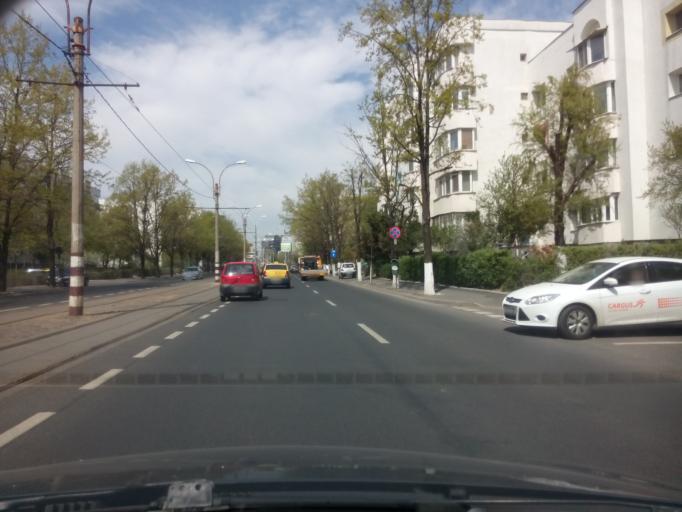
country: RO
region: Bucuresti
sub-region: Municipiul Bucuresti
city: Bucharest
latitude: 44.4847
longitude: 26.0965
